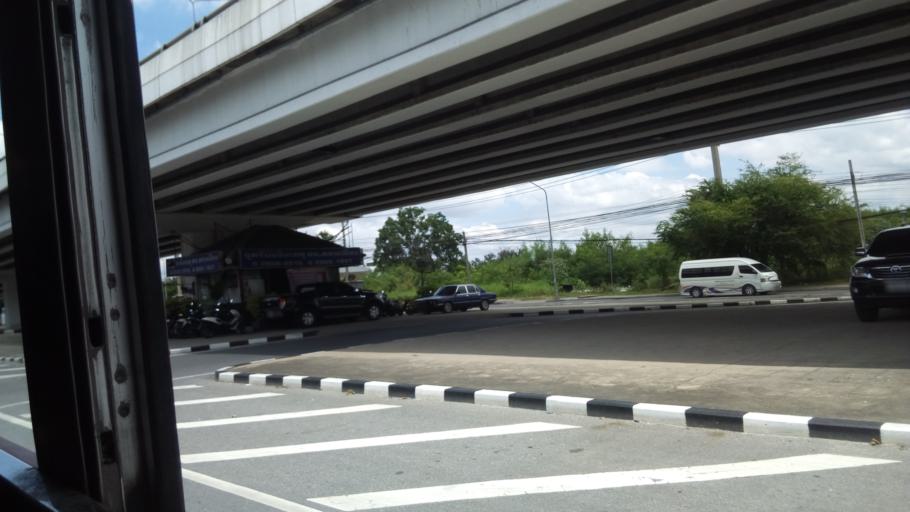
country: TH
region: Bangkok
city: Sai Mai
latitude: 13.9465
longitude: 100.6233
